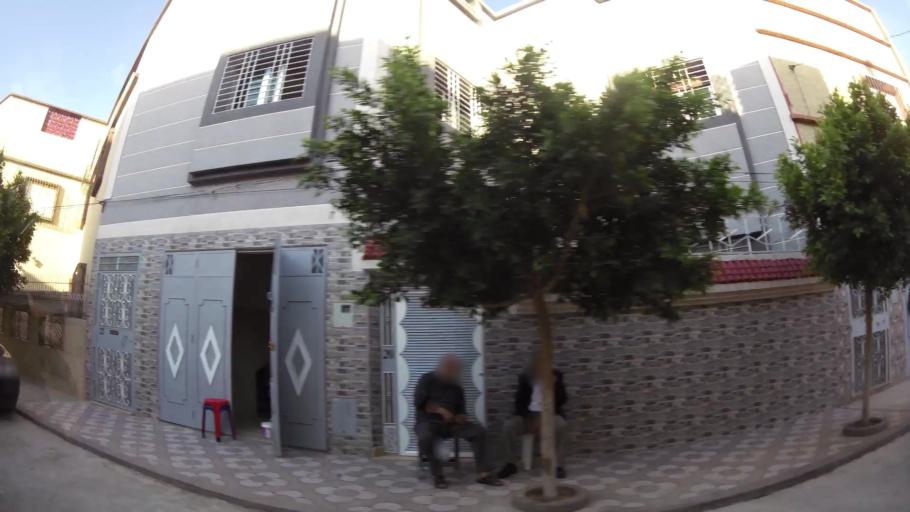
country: MA
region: Oriental
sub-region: Oujda-Angad
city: Oujda
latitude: 34.7041
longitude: -1.8977
